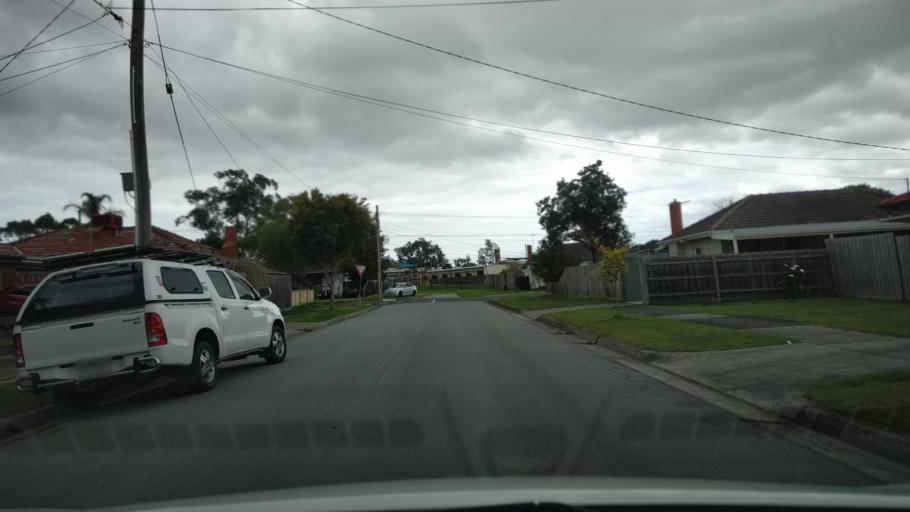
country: AU
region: Victoria
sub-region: Greater Dandenong
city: Noble Park
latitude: -37.9718
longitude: 145.1811
